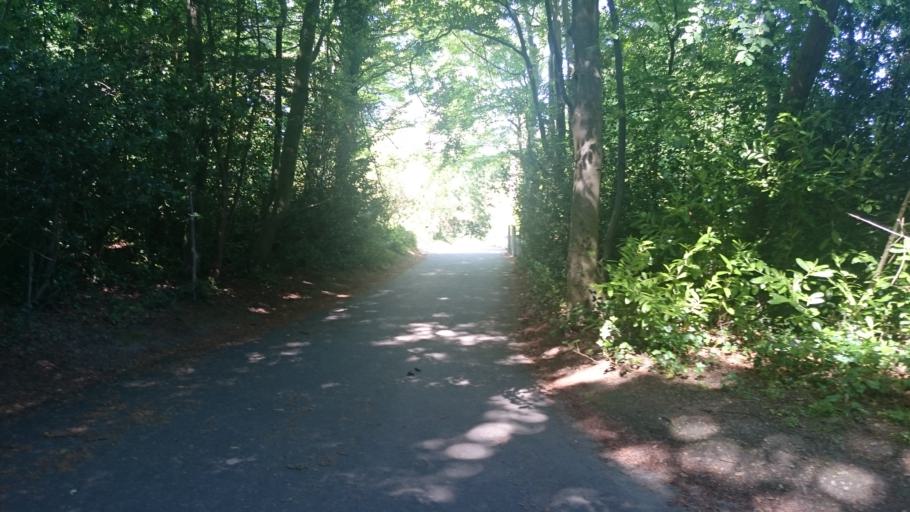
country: IE
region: Leinster
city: Ballinteer
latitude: 53.2741
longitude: -6.2684
